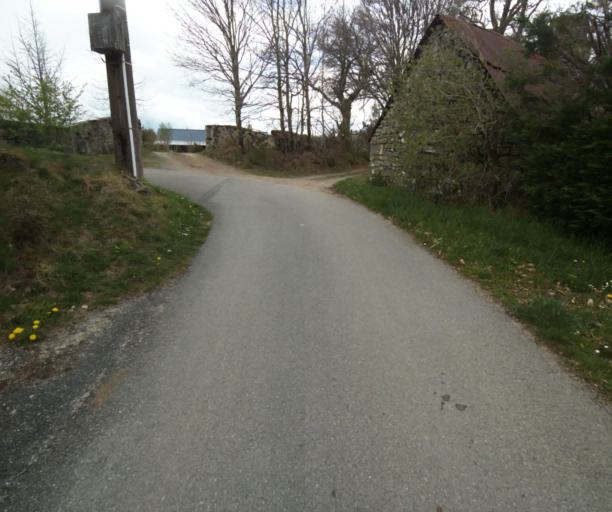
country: FR
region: Limousin
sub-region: Departement de la Correze
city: Correze
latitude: 45.2920
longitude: 1.9288
